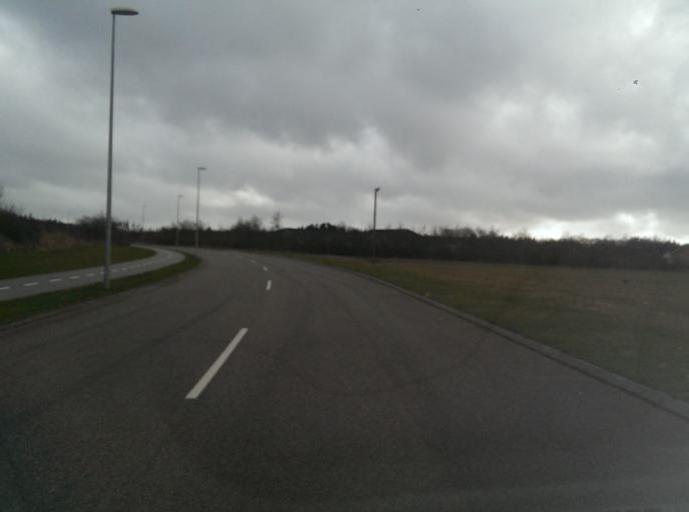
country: DK
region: Central Jutland
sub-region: Holstebro Kommune
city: Ulfborg
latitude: 56.2760
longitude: 8.3065
